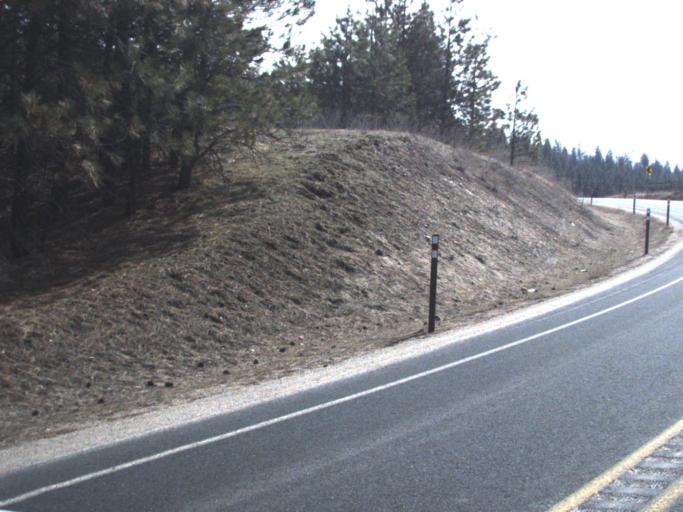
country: US
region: Washington
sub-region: Stevens County
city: Colville
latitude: 48.5109
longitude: -117.7292
